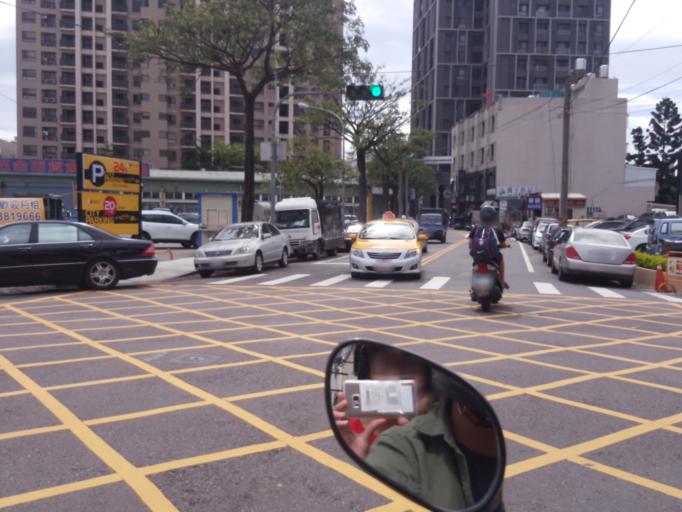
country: TW
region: Taiwan
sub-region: Taichung City
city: Taichung
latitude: 24.1096
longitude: 120.6920
